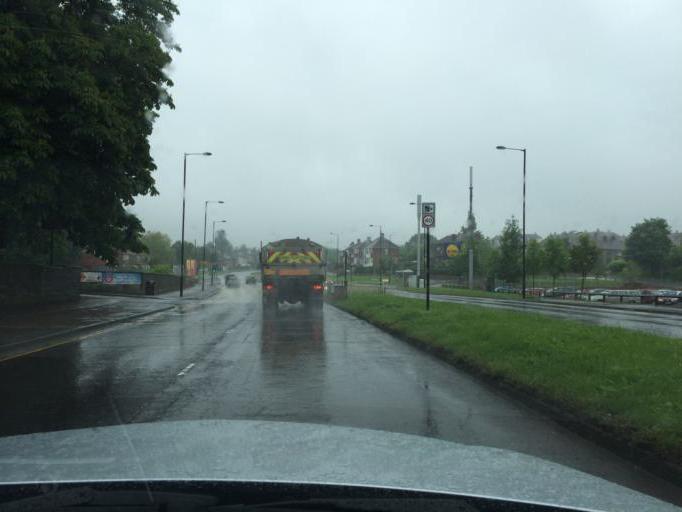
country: GB
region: England
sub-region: Sheffield
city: Chapletown
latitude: 53.4224
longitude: -1.4924
